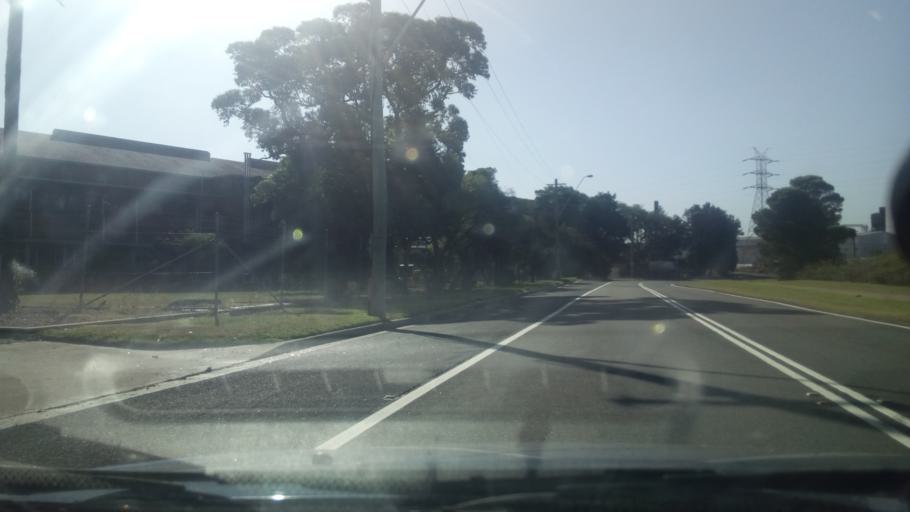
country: AU
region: New South Wales
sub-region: Wollongong
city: Port Kembla
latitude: -34.4735
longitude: 150.9002
